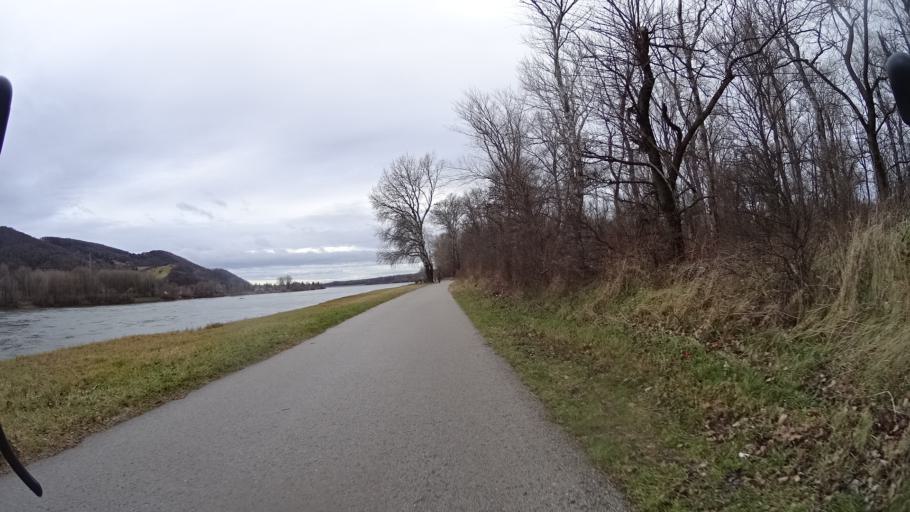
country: AT
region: Lower Austria
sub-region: Politischer Bezirk Korneuburg
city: Korneuburg
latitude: 48.3472
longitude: 16.3001
